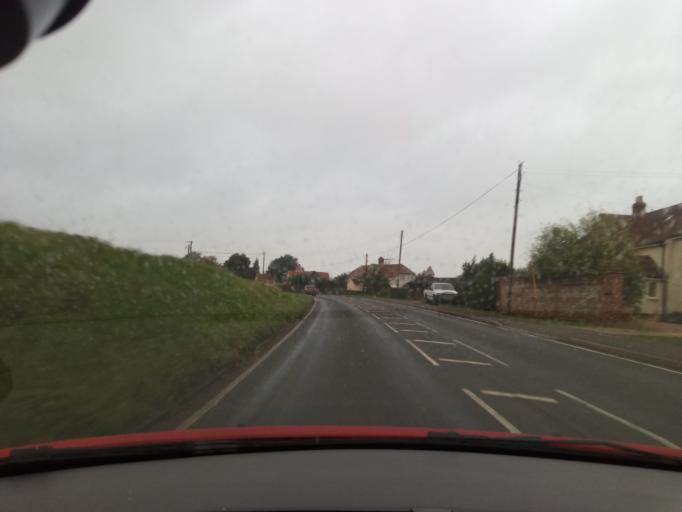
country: GB
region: England
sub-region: Suffolk
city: Kedington
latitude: 52.0652
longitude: 0.4830
